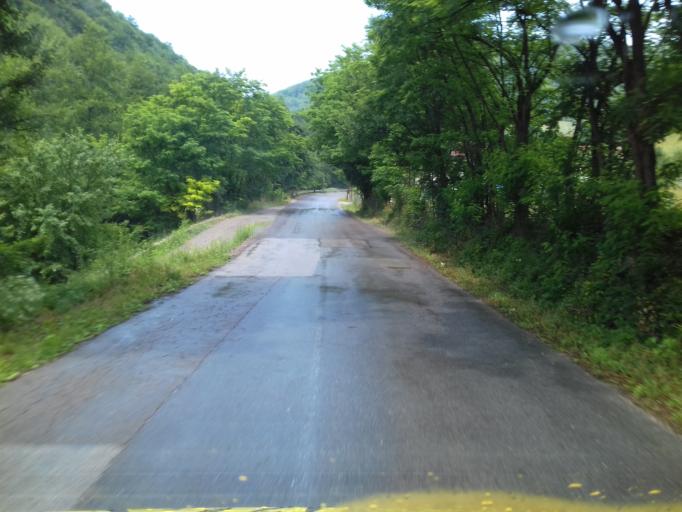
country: BA
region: Federation of Bosnia and Herzegovina
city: Kiseljak
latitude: 43.9549
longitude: 18.1152
